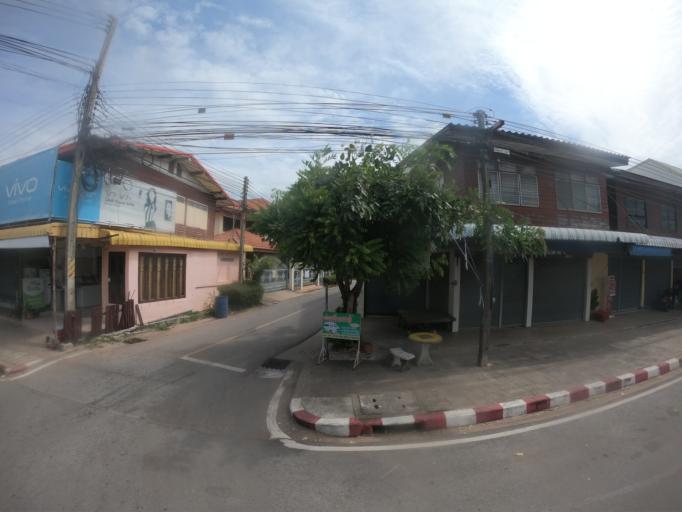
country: TH
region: Maha Sarakham
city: Chiang Yuen
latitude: 16.4085
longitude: 103.0980
